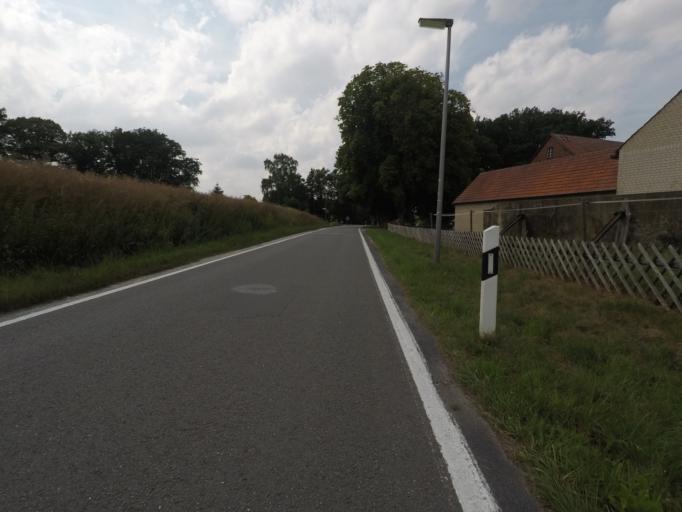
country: DE
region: North Rhine-Westphalia
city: Enger
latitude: 52.1637
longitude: 8.5494
